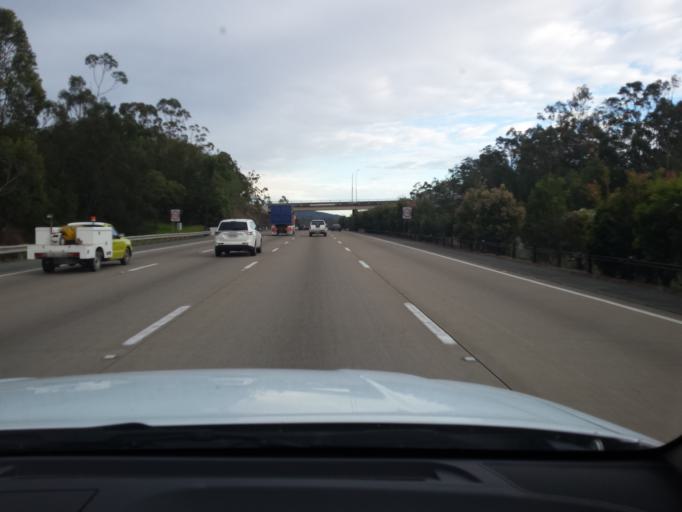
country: AU
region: Queensland
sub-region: Gold Coast
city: Ormeau Hills
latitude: -27.8216
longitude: 153.2909
